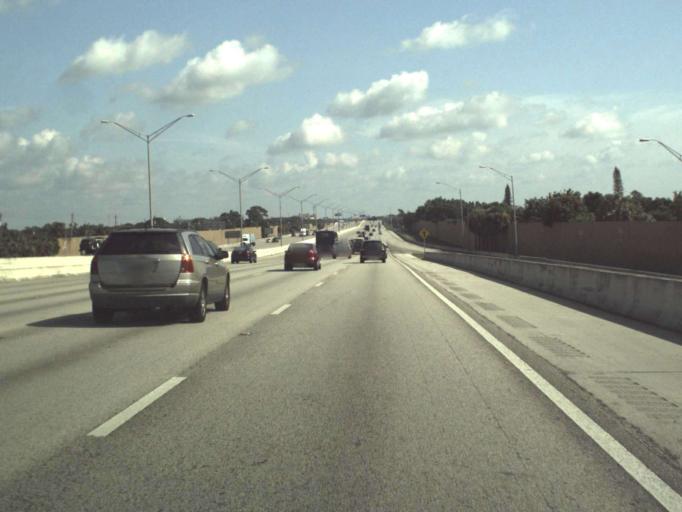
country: US
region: Florida
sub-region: Palm Beach County
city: North Palm Beach
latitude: 26.8105
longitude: -80.0979
